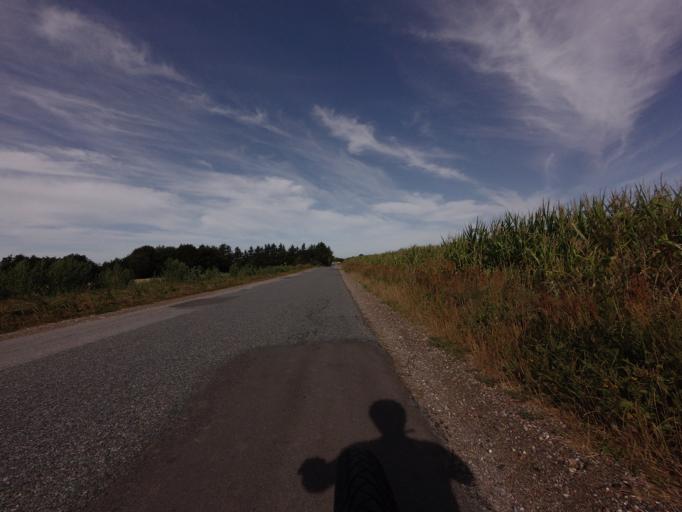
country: DK
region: North Denmark
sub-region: Hjorring Kommune
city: Vra
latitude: 57.4088
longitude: 9.9120
